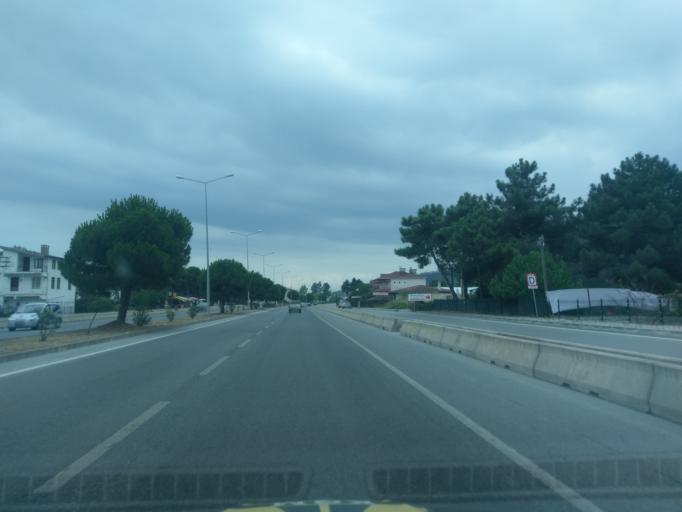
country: TR
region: Samsun
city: Taflan
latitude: 41.3970
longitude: 36.1963
